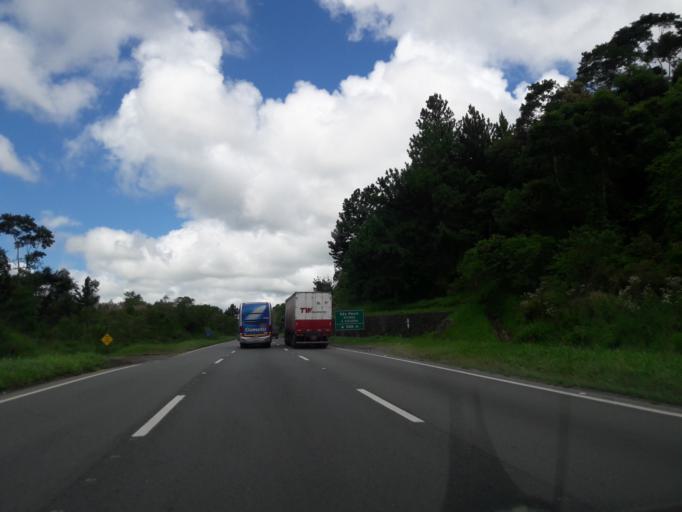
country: BR
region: Sao Paulo
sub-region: Cajati
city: Cajati
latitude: -24.9807
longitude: -48.5062
